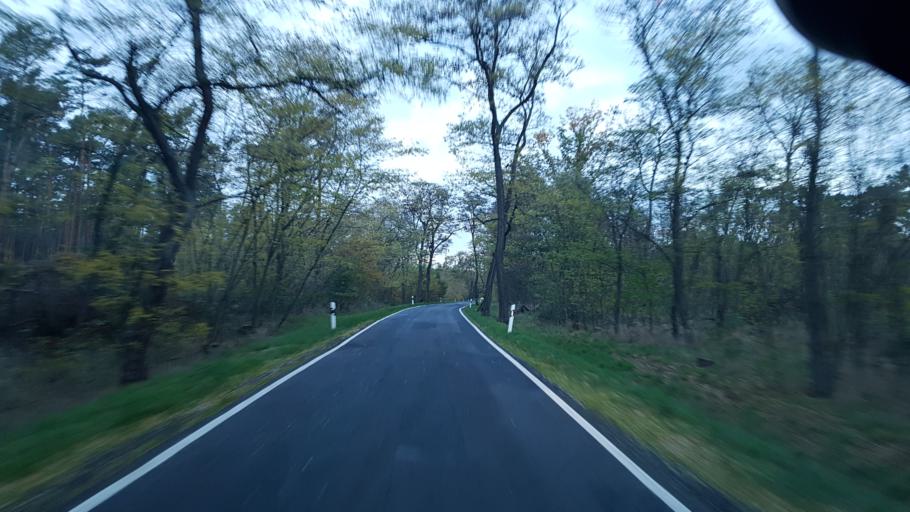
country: DE
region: Brandenburg
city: Muhlberg
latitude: 51.4734
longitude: 13.2392
